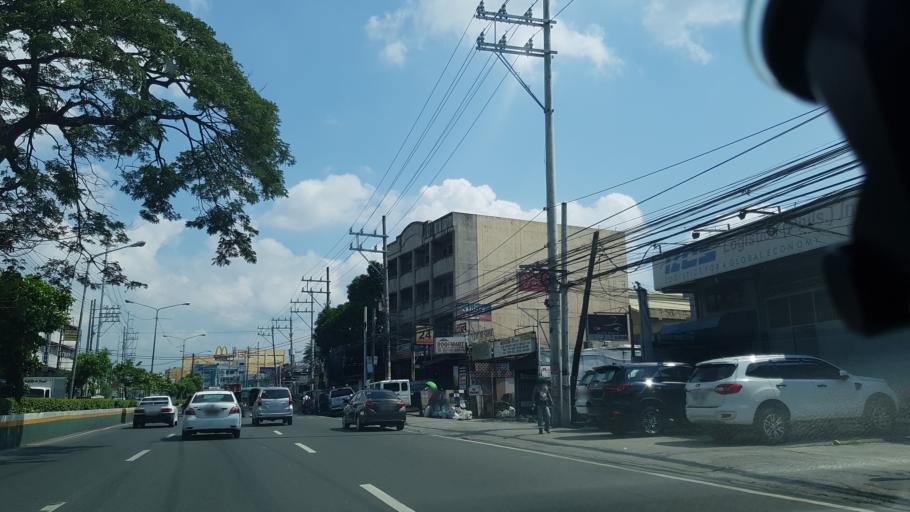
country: PH
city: Sambayanihan People's Village
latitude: 14.4782
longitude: 120.9985
